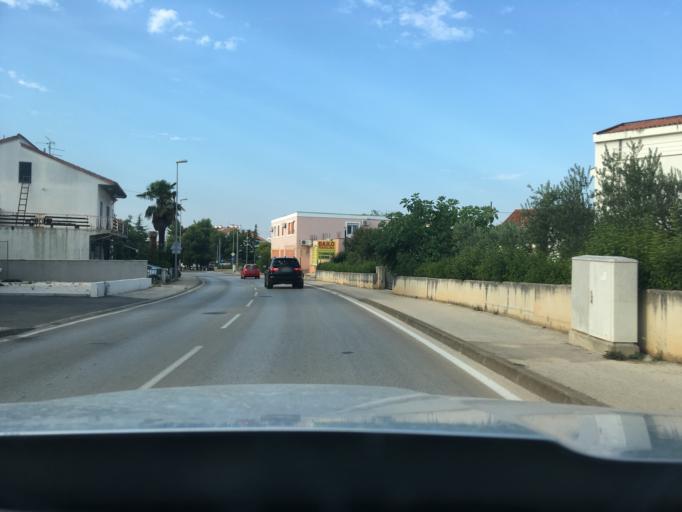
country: HR
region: Zadarska
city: Zadar
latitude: 44.1322
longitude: 15.2306
